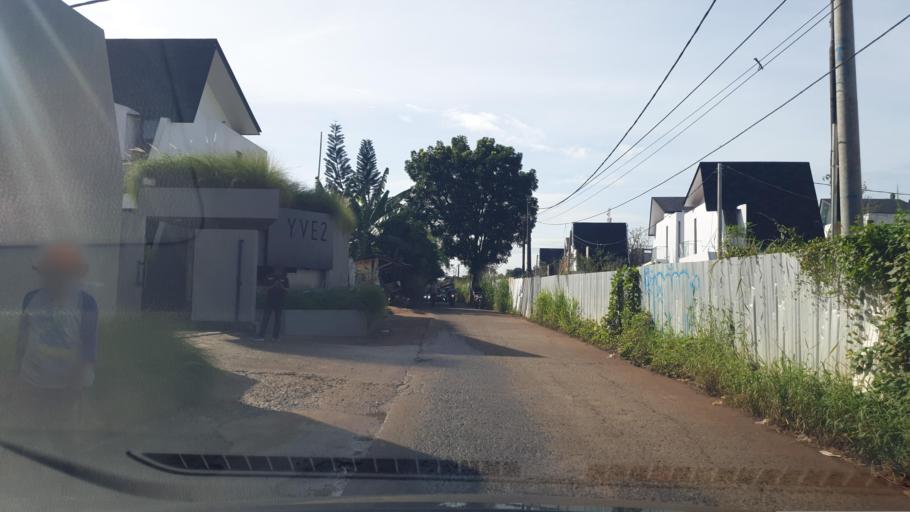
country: ID
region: West Java
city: Sawangan
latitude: -6.3728
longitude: 106.7849
